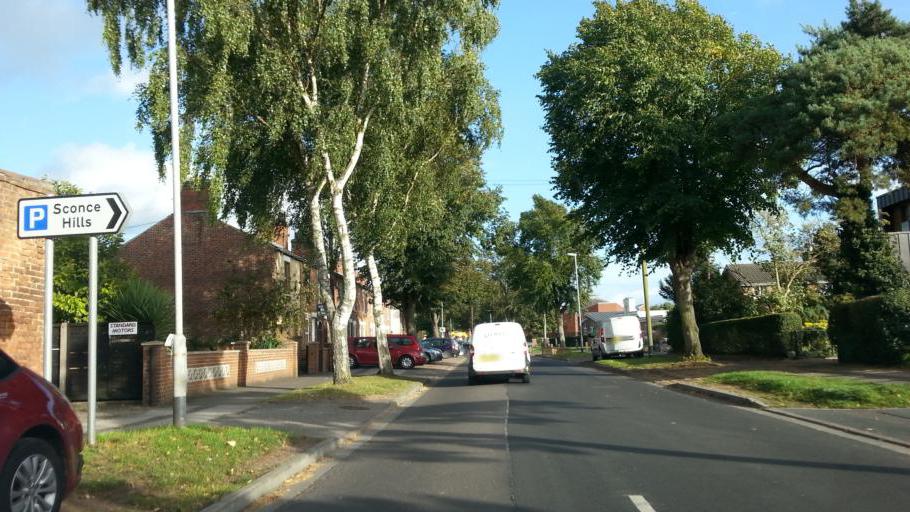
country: GB
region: England
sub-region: Nottinghamshire
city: Newark on Trent
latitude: 53.0713
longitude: -0.8182
